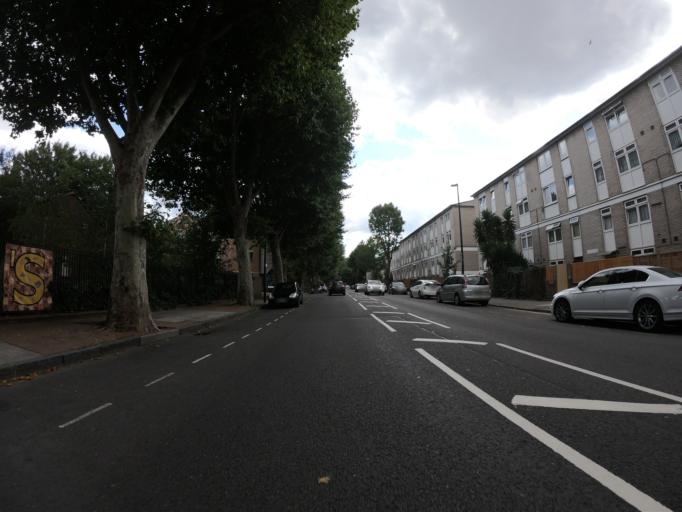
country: GB
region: England
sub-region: Greater London
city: Poplar
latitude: 51.4902
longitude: -0.0061
